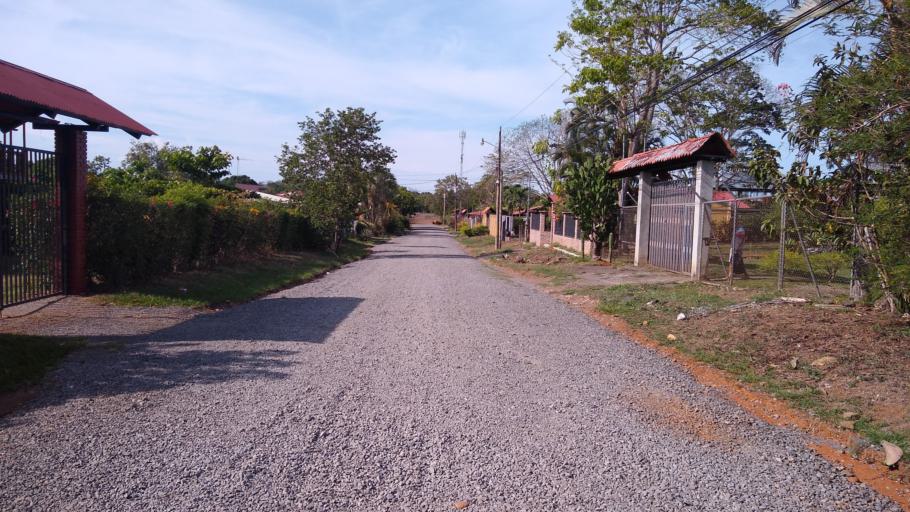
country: CR
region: Puntarenas
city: Esparza
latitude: 9.9945
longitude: -84.6435
